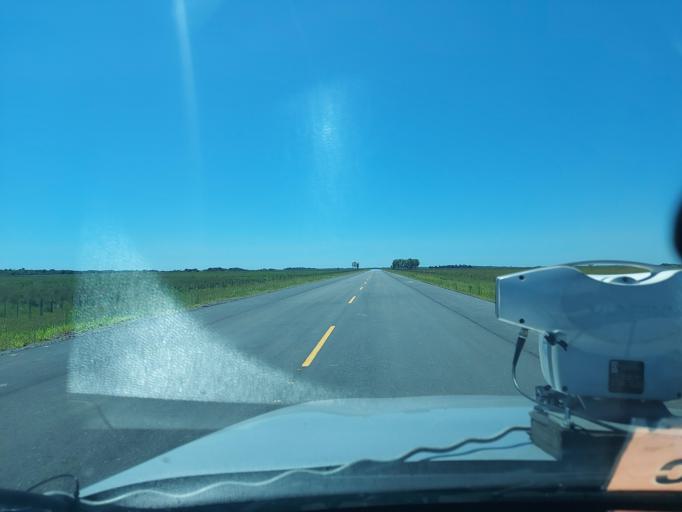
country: PY
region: Neembucu
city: Pilar
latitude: -26.8203
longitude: -58.2514
